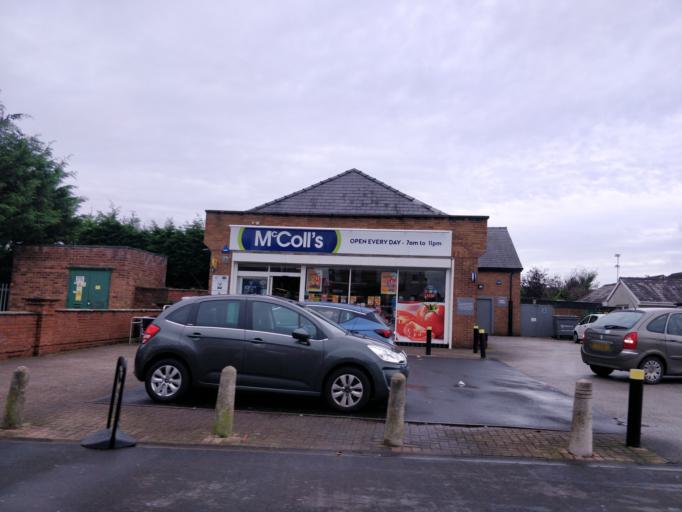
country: GB
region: England
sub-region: Sefton
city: Southport
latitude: 53.6676
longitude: -2.9708
